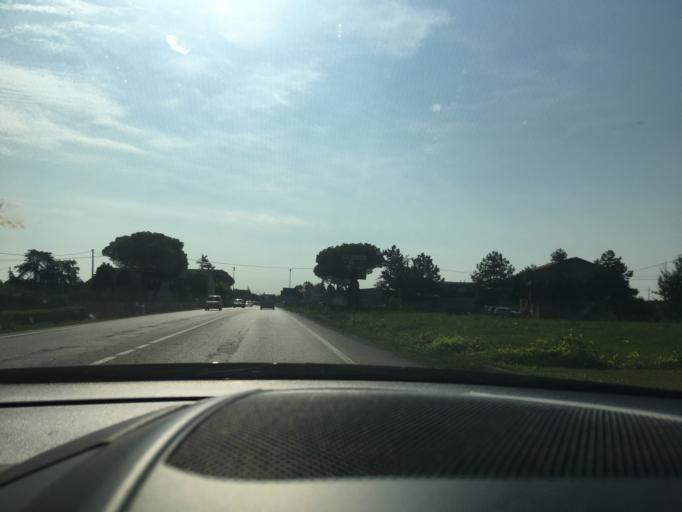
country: IT
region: Emilia-Romagna
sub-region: Provincia di Rimini
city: Santa Giustina
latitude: 44.1048
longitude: 12.4884
